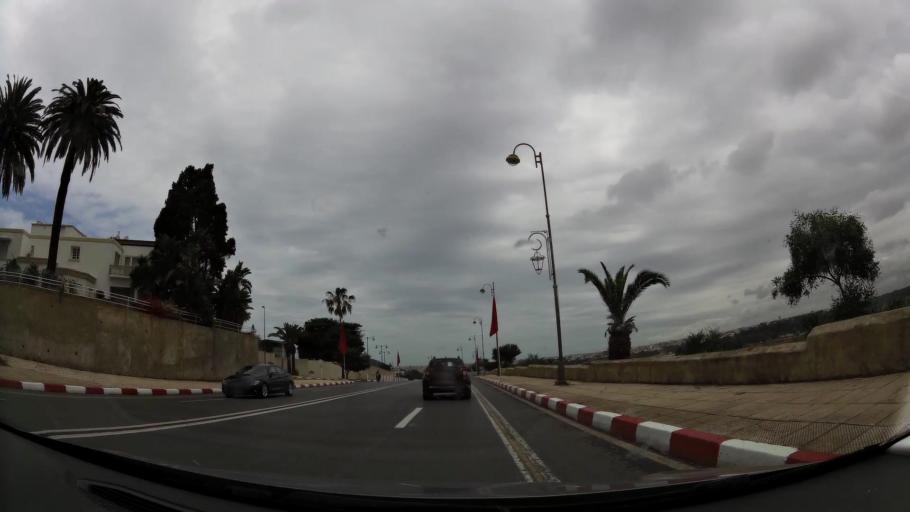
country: MA
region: Rabat-Sale-Zemmour-Zaer
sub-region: Rabat
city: Rabat
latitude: 34.0139
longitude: -6.8197
